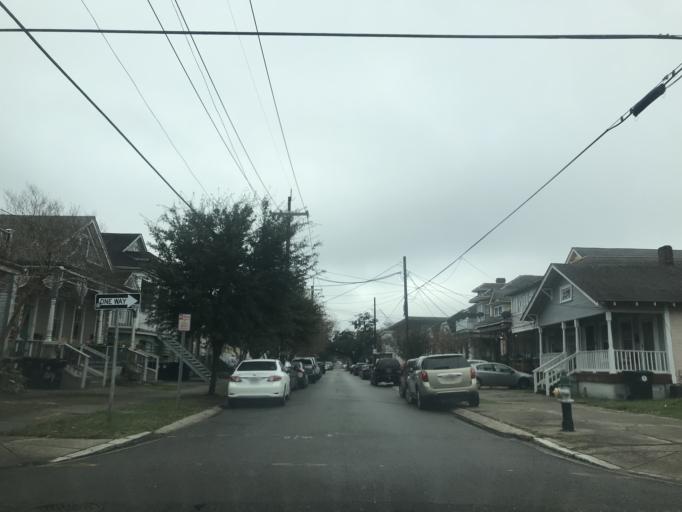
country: US
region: Louisiana
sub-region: Orleans Parish
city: New Orleans
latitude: 29.9716
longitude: -90.0984
